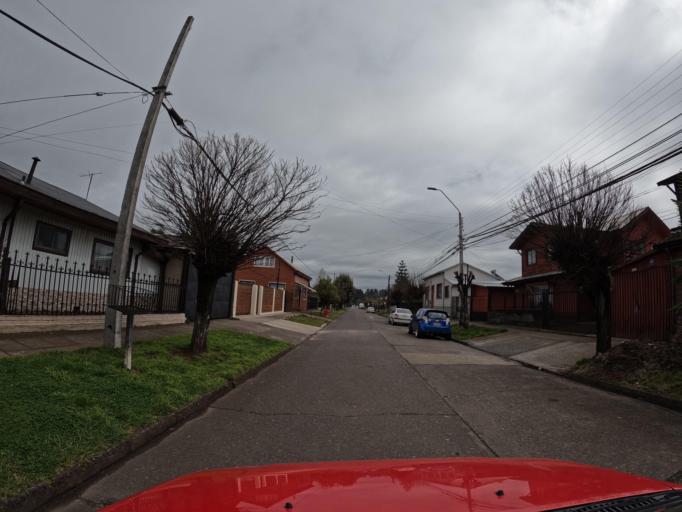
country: CL
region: Araucania
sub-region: Provincia de Malleco
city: Victoria
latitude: -38.2314
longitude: -72.3338
